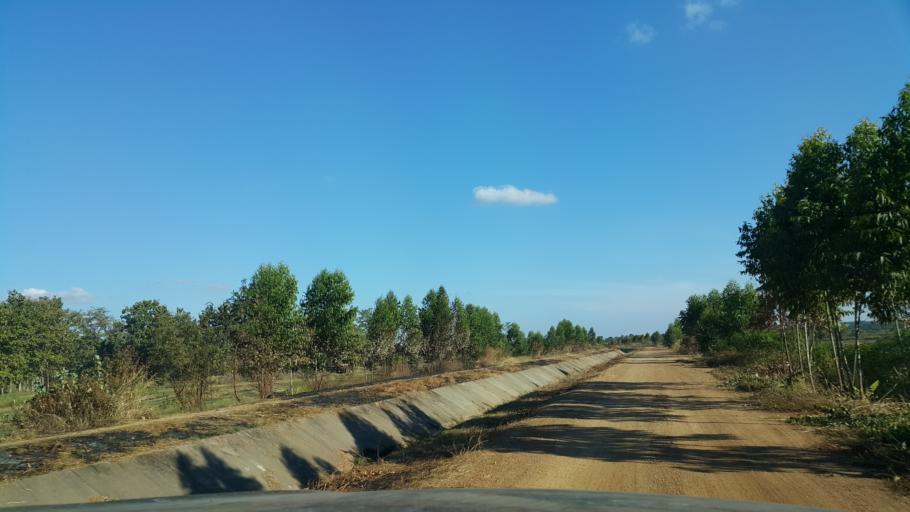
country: TH
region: Sukhothai
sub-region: Amphoe Si Satchanalai
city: Si Satchanalai
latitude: 17.4821
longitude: 99.6510
